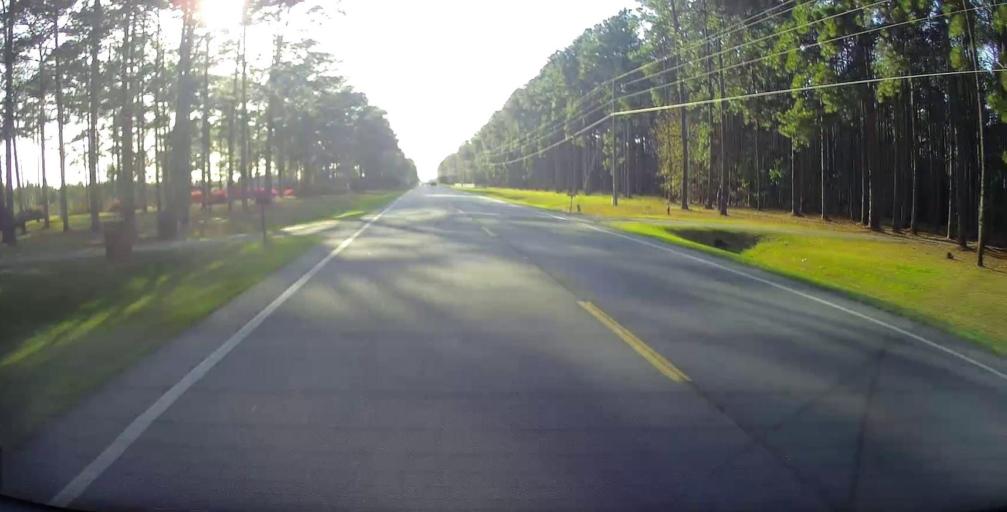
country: US
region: Georgia
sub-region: Evans County
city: Claxton
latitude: 32.1497
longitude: -81.9800
